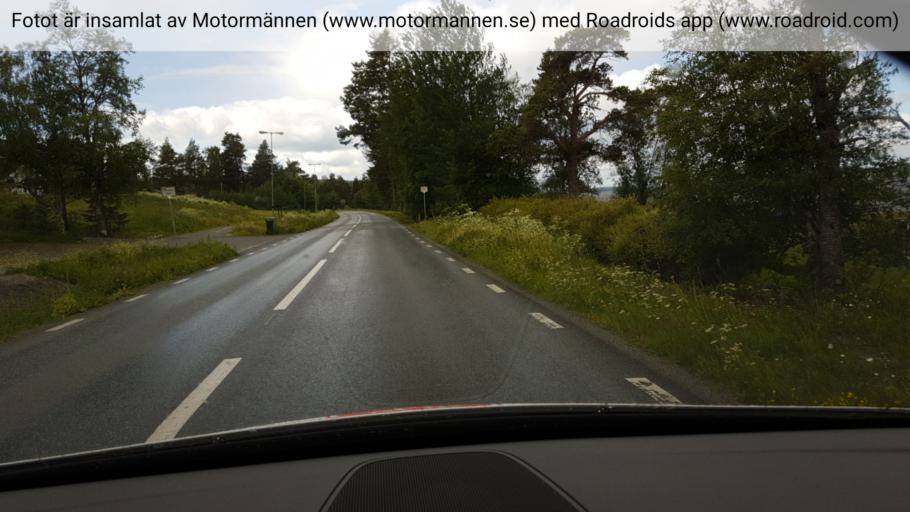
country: SE
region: Jaemtland
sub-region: OEstersunds Kommun
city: Ostersund
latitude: 63.1530
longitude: 14.5617
